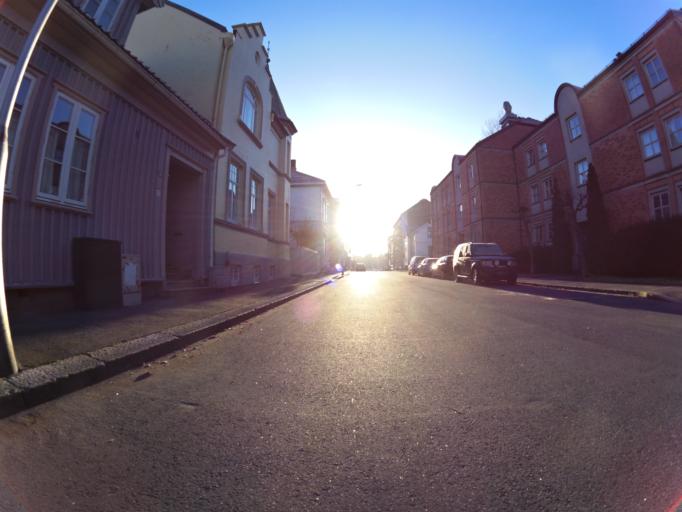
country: NO
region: Ostfold
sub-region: Fredrikstad
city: Fredrikstad
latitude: 59.2064
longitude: 10.9443
